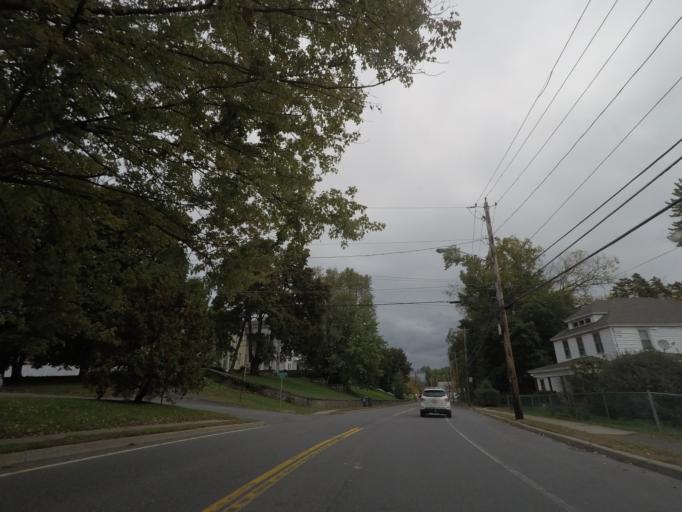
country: US
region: New York
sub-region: Albany County
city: Cohoes
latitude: 42.7867
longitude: -73.6939
